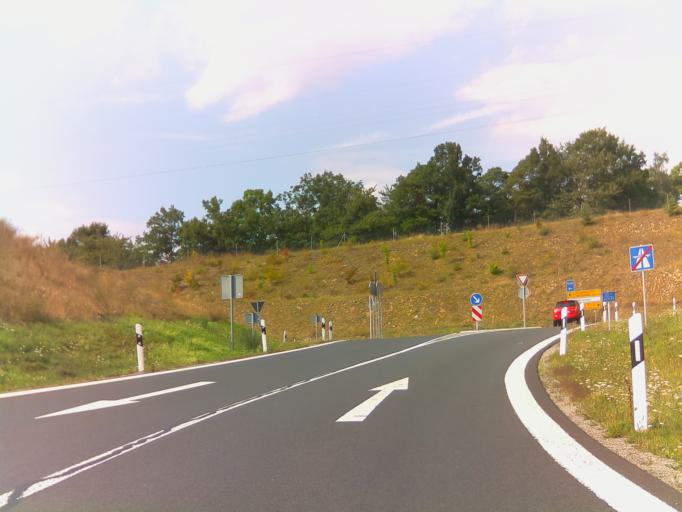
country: DE
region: Bavaria
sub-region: Regierungsbezirk Unterfranken
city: Rodelmaier
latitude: 50.3297
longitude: 10.2900
